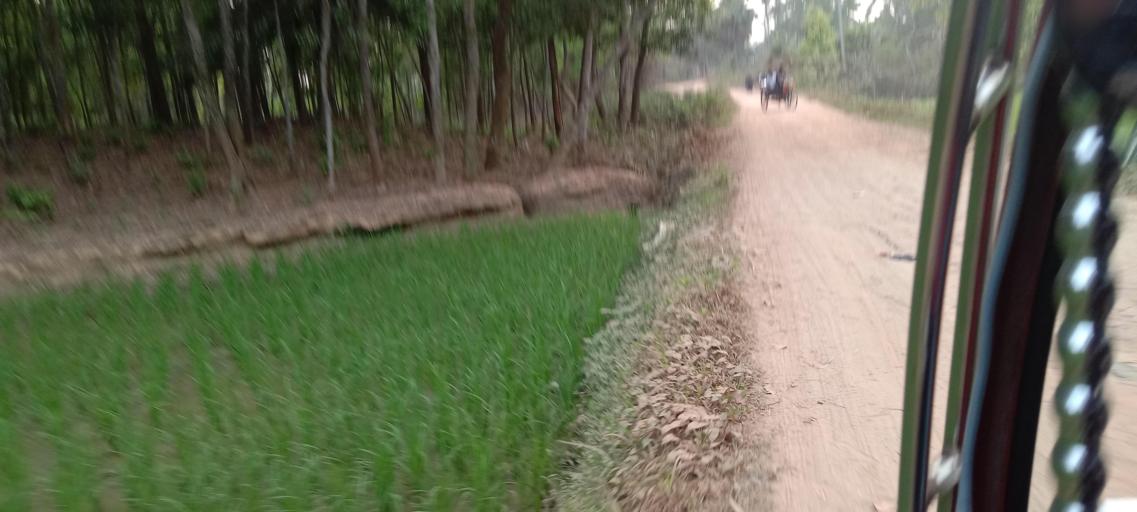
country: BD
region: Dhaka
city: Sakhipur
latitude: 24.4274
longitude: 90.2432
